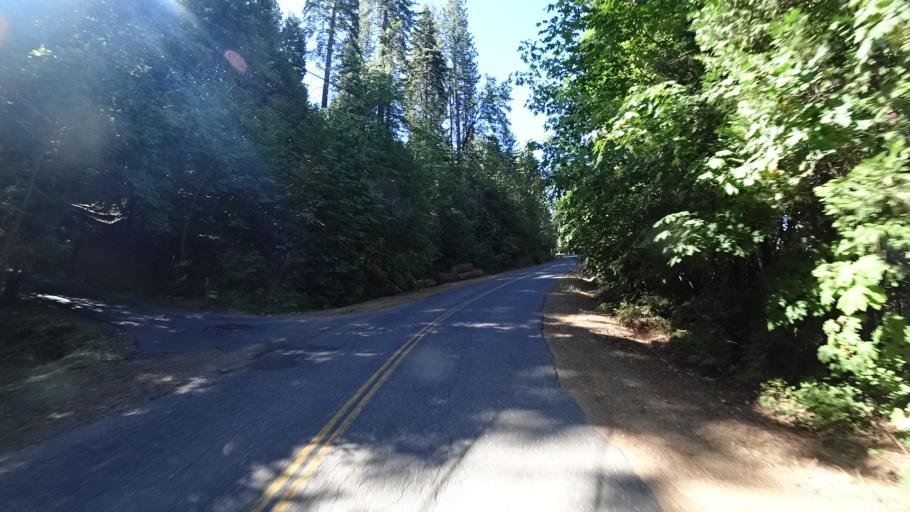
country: US
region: California
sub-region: Calaveras County
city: Arnold
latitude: 38.2583
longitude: -120.3232
